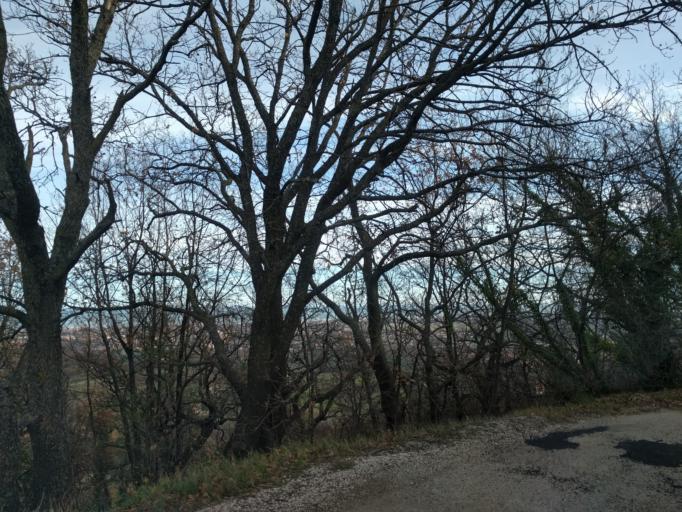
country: IT
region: The Marches
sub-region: Provincia di Pesaro e Urbino
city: Centinarola
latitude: 43.8196
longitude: 12.9742
